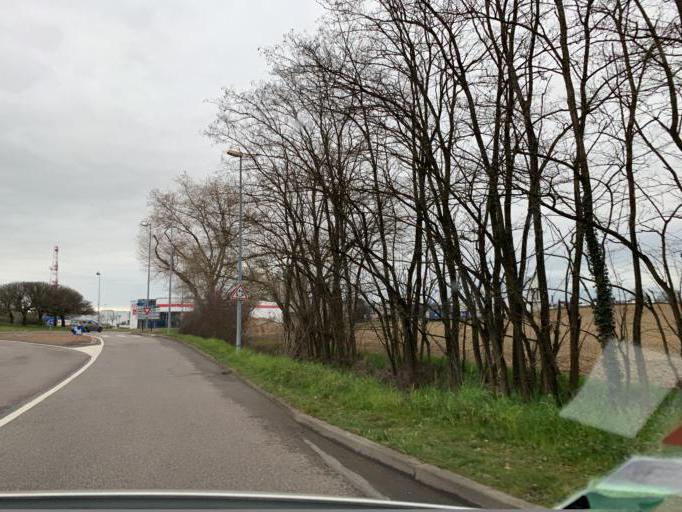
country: FR
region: Rhone-Alpes
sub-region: Departement du Rhone
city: Rillieux-la-Pape
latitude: 45.8304
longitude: 4.9072
